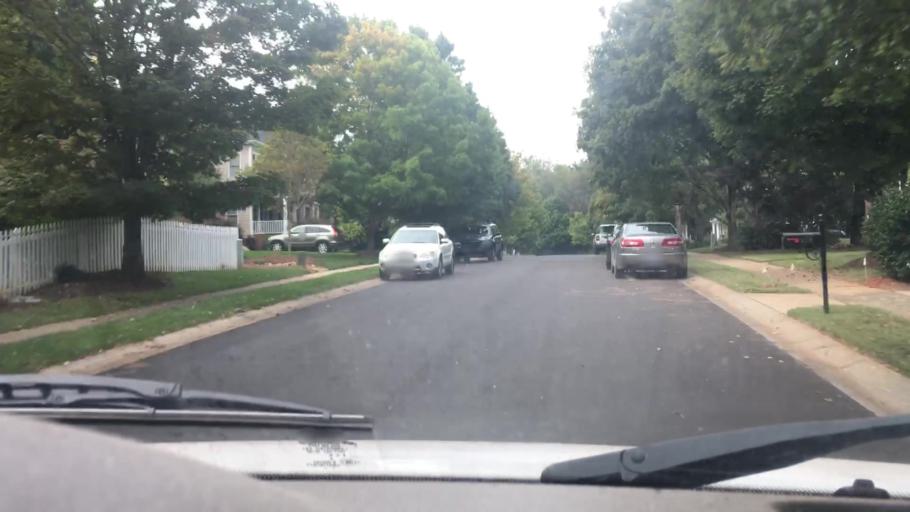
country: US
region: North Carolina
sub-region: Gaston County
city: Davidson
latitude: 35.4915
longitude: -80.8293
